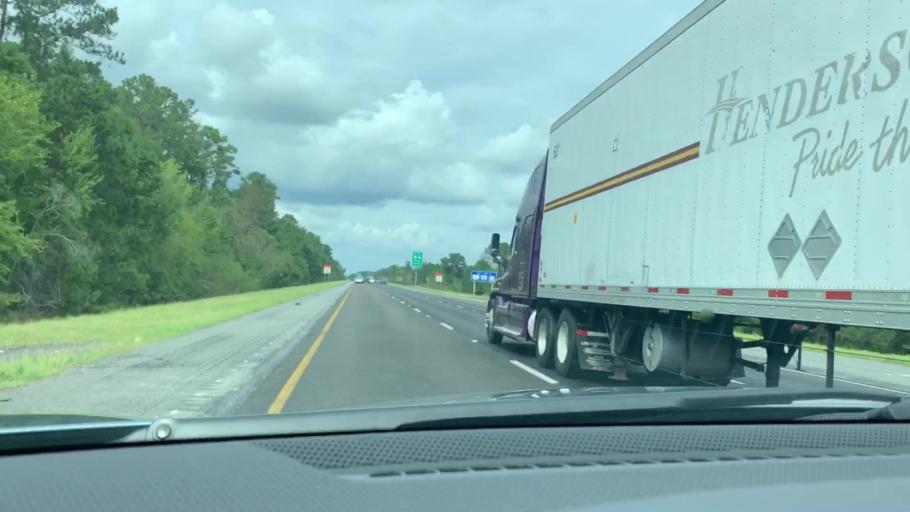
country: US
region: Georgia
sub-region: Liberty County
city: Midway
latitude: 31.7574
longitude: -81.3823
